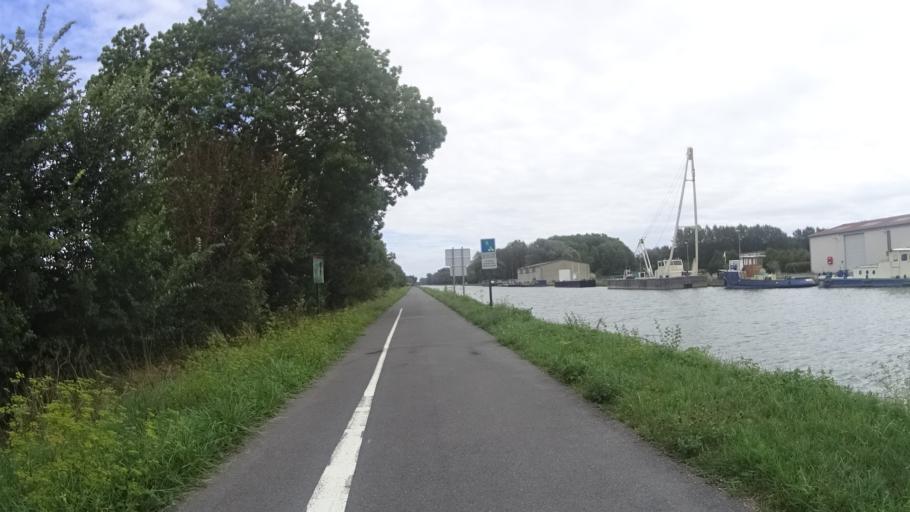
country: FR
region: Picardie
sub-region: Departement de l'Oise
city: Noyon
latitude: 49.5624
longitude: 2.9950
